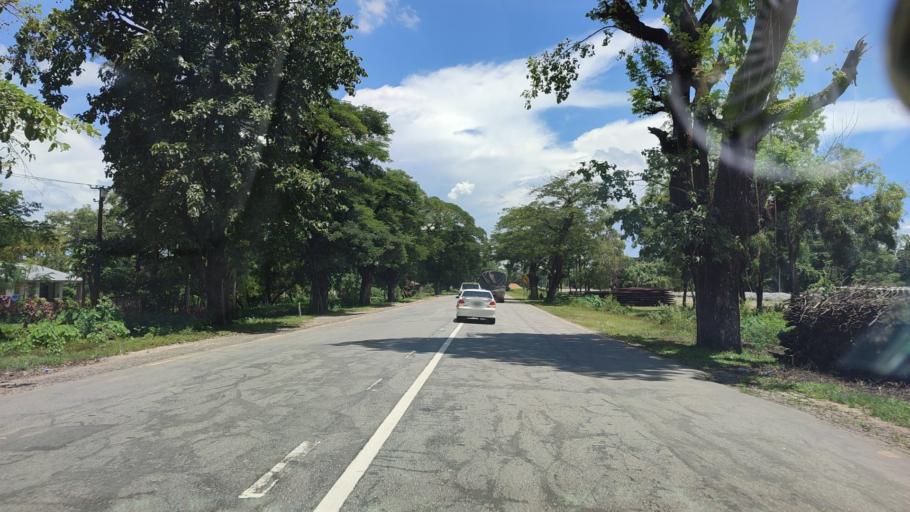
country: MM
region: Bago
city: Nyaunglebin
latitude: 18.1637
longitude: 96.6060
